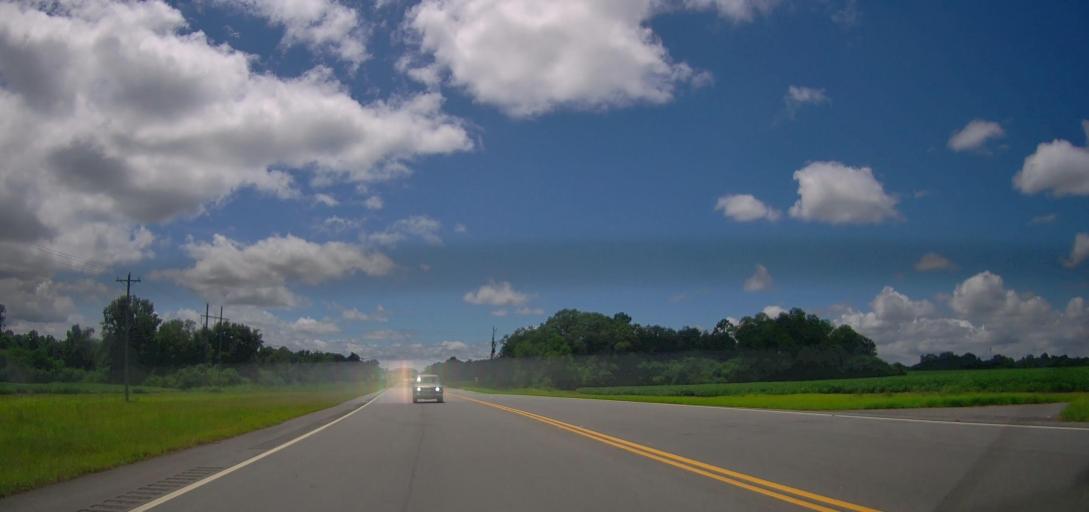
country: US
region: Georgia
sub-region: Turner County
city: Ashburn
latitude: 31.7153
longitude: -83.6268
